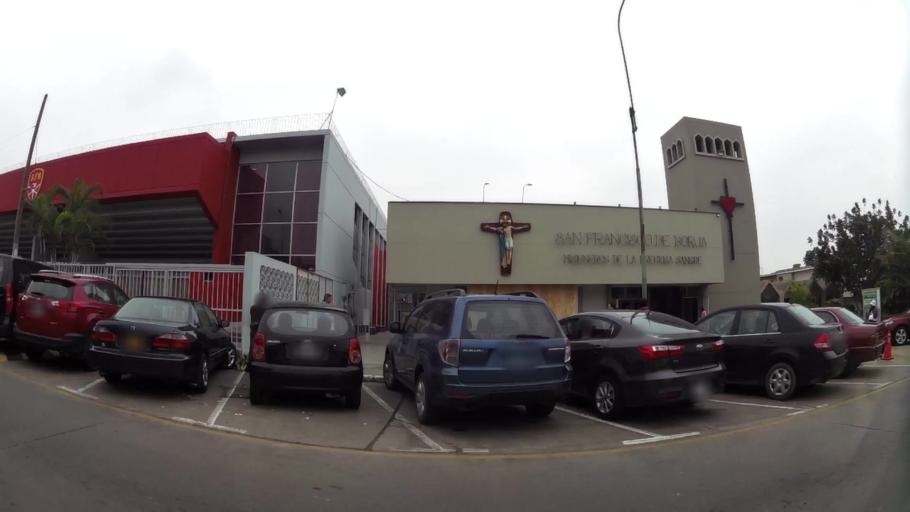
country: PE
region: Lima
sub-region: Lima
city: San Luis
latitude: -12.0900
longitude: -76.9980
